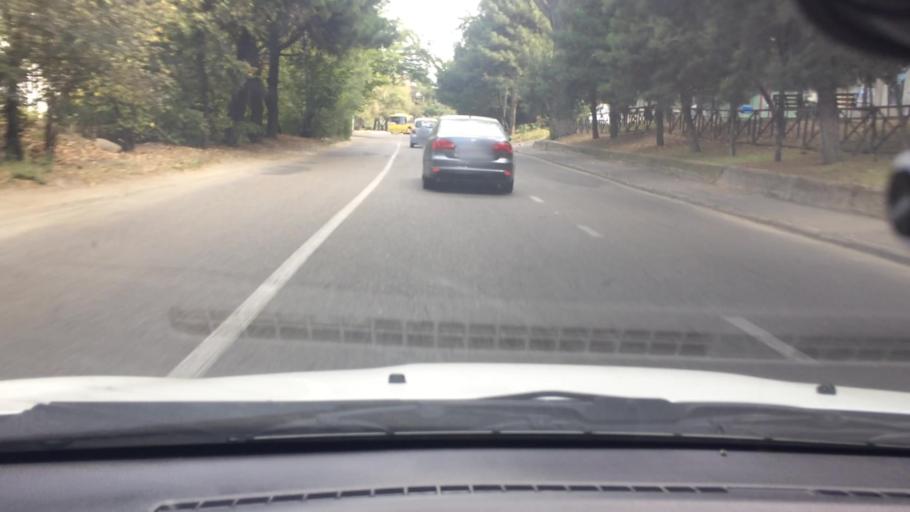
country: GE
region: T'bilisi
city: Tbilisi
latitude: 41.6709
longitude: 44.8441
